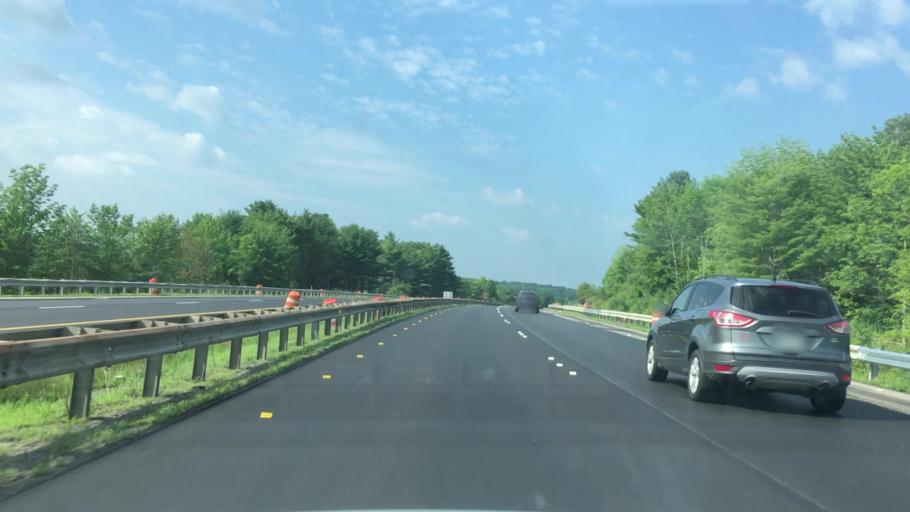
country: US
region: Maine
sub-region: Androscoggin County
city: Lewiston
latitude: 44.0576
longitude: -70.2155
